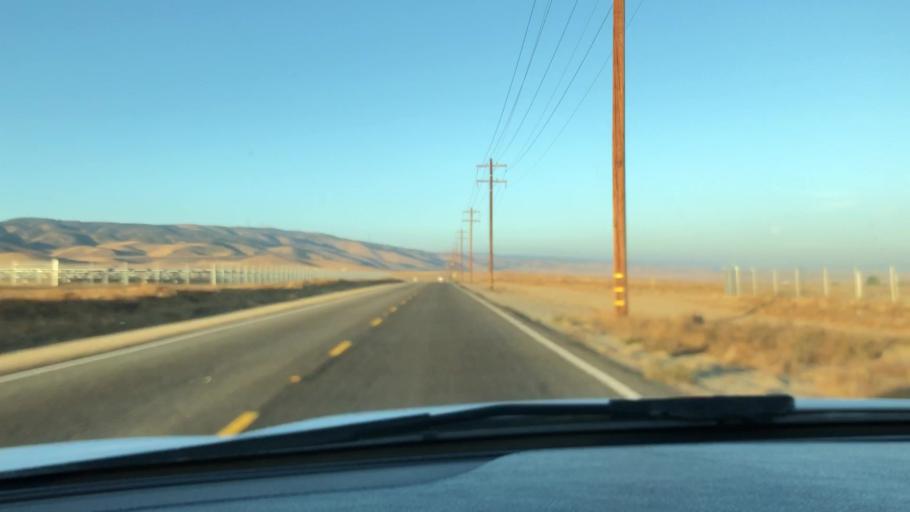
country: US
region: California
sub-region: Los Angeles County
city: Leona Valley
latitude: 34.6747
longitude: -118.3189
